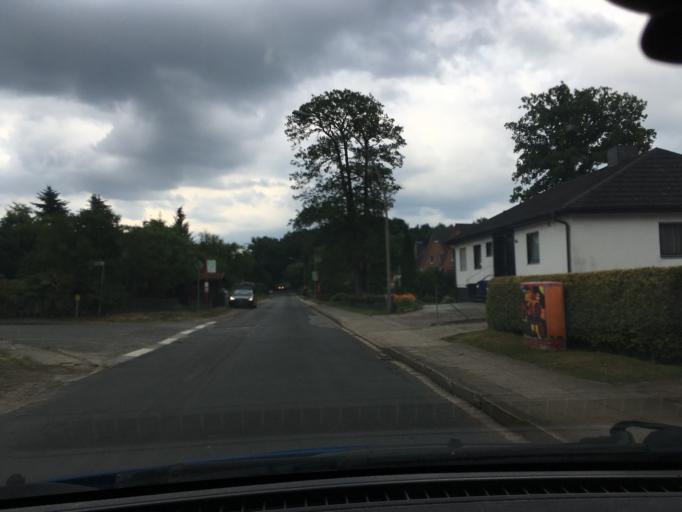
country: DE
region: Lower Saxony
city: Tostedt
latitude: 53.2828
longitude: 9.7440
